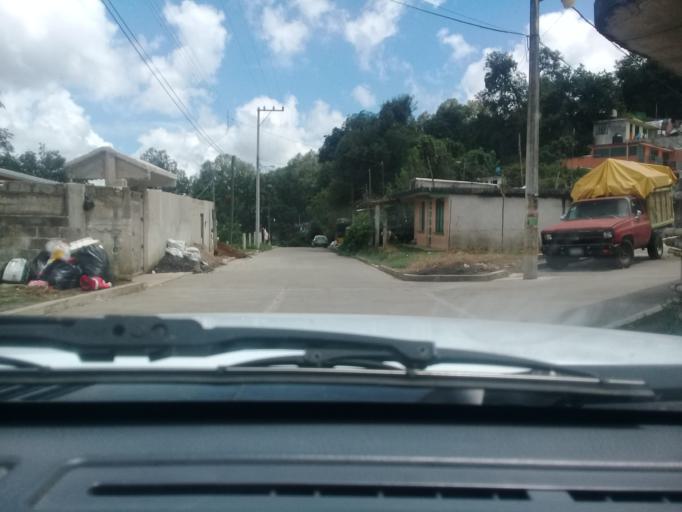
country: MX
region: Veracruz
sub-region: Tlalnelhuayocan
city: Otilpan
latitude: 19.5382
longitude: -96.9729
